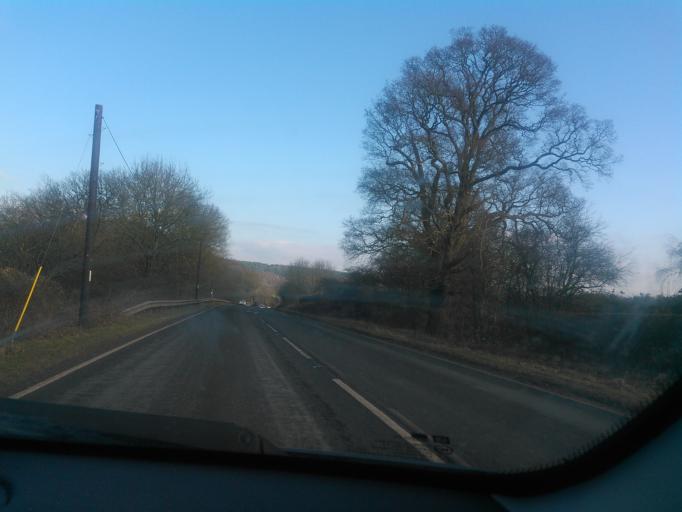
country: GB
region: England
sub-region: Shropshire
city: Wem
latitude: 52.8335
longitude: -2.6775
